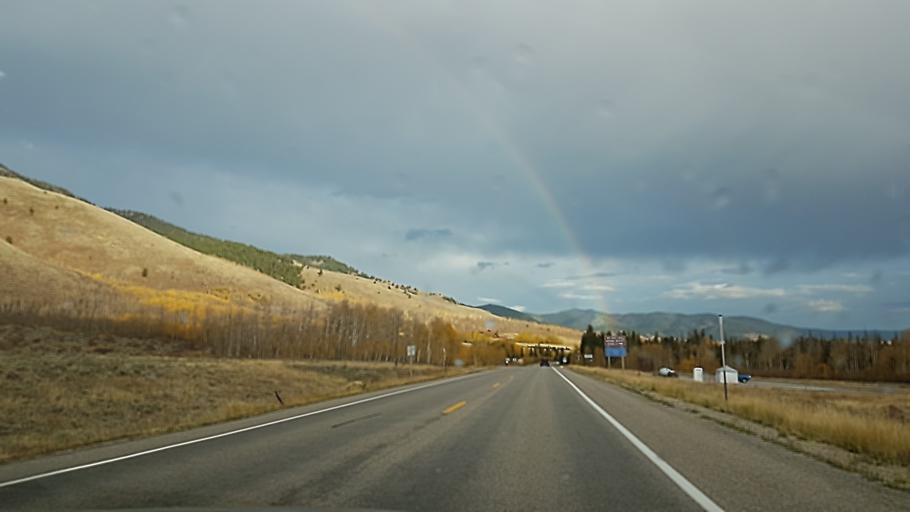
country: US
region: Montana
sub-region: Gallatin County
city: West Yellowstone
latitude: 44.6741
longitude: -111.4111
